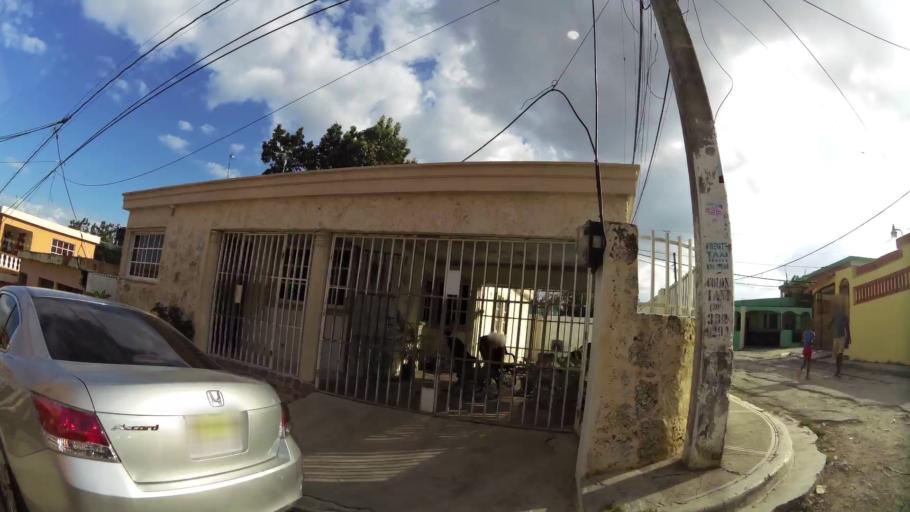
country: DO
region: Nacional
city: Ensanche Luperon
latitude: 18.5535
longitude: -69.8957
